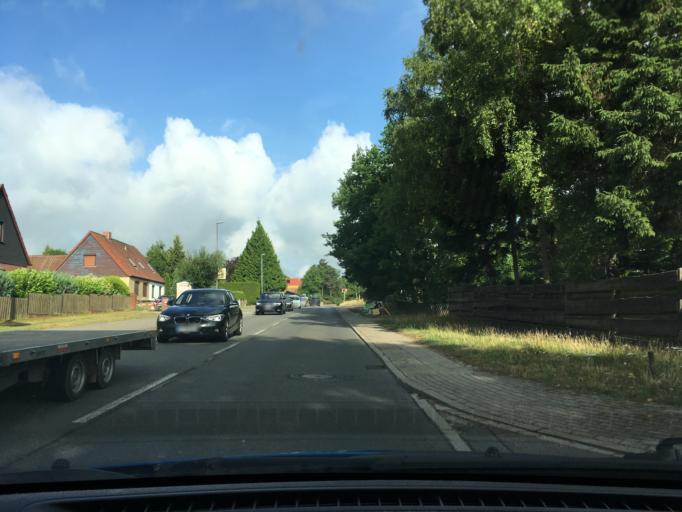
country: DE
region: Lower Saxony
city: Buchholz in der Nordheide
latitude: 53.3240
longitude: 9.8534
